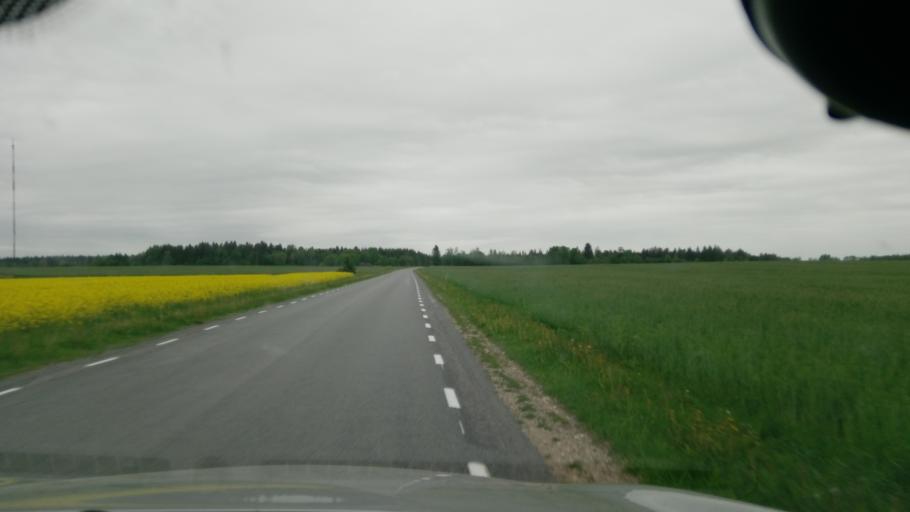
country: EE
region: Jaervamaa
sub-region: Koeru vald
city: Koeru
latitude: 58.9941
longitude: 26.0614
